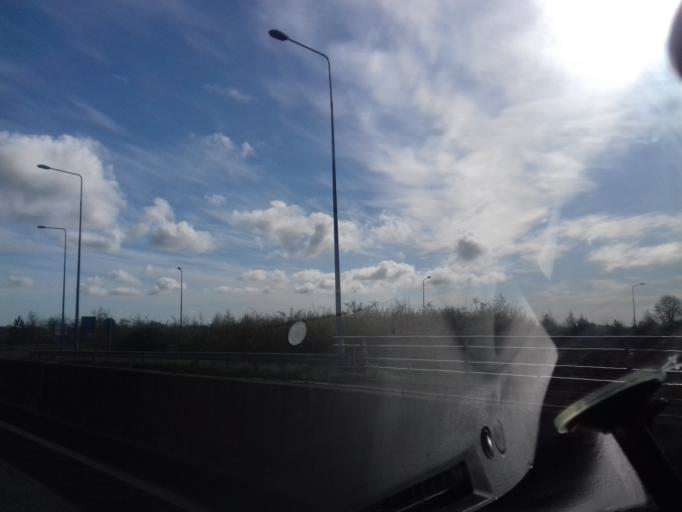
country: IE
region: Leinster
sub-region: An Mhi
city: Kells
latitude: 53.7088
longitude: -6.8566
